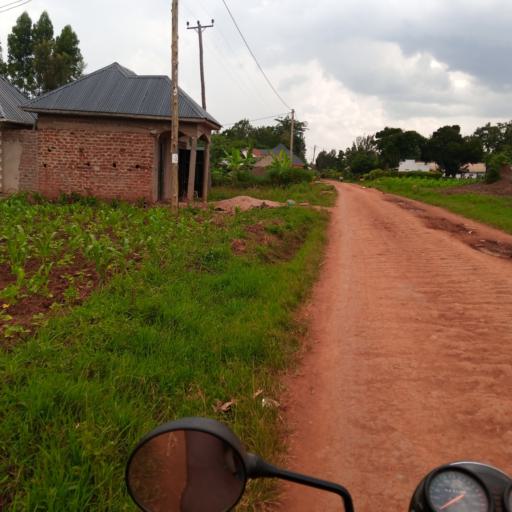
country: UG
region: Eastern Region
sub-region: Mbale District
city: Mbale
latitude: 1.1104
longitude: 34.1835
